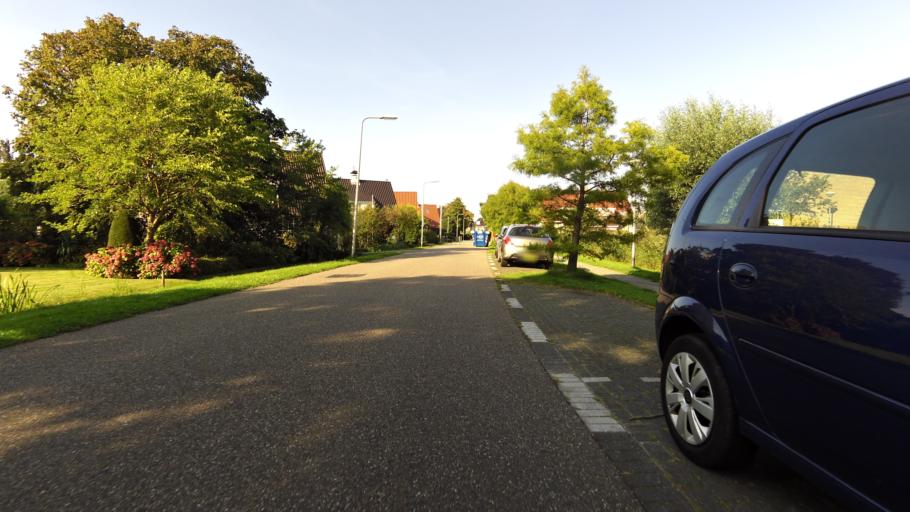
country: NL
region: South Holland
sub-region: Gemeente Katwijk
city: Rijnsburg
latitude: 52.1859
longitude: 4.4374
